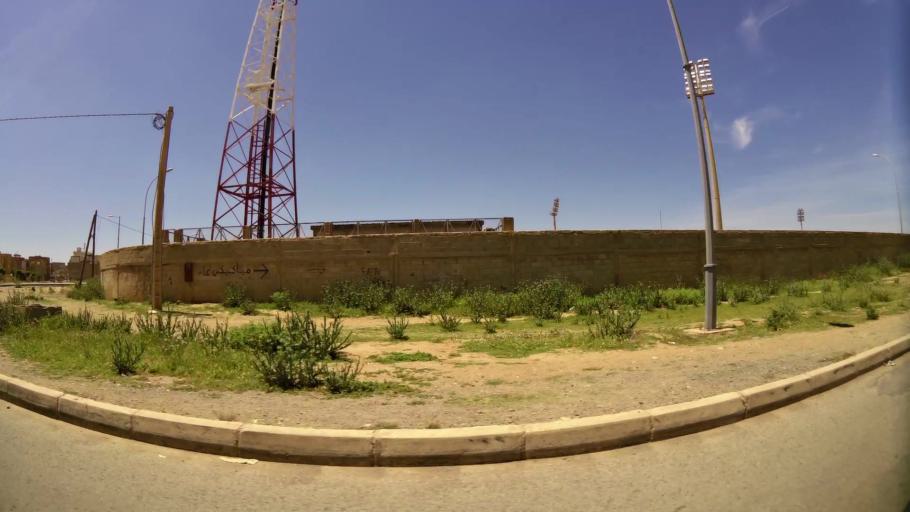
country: MA
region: Oriental
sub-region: Oujda-Angad
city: Oujda
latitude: 34.6589
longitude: -1.9330
